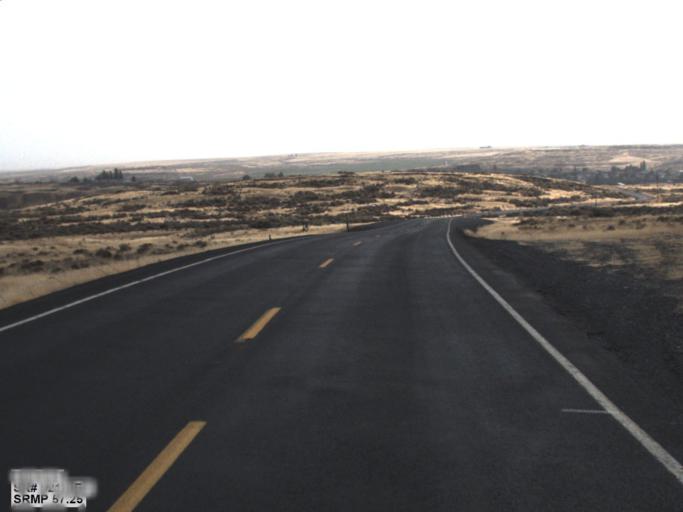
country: US
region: Washington
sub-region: Adams County
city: Ritzville
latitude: 47.3504
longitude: -118.6954
